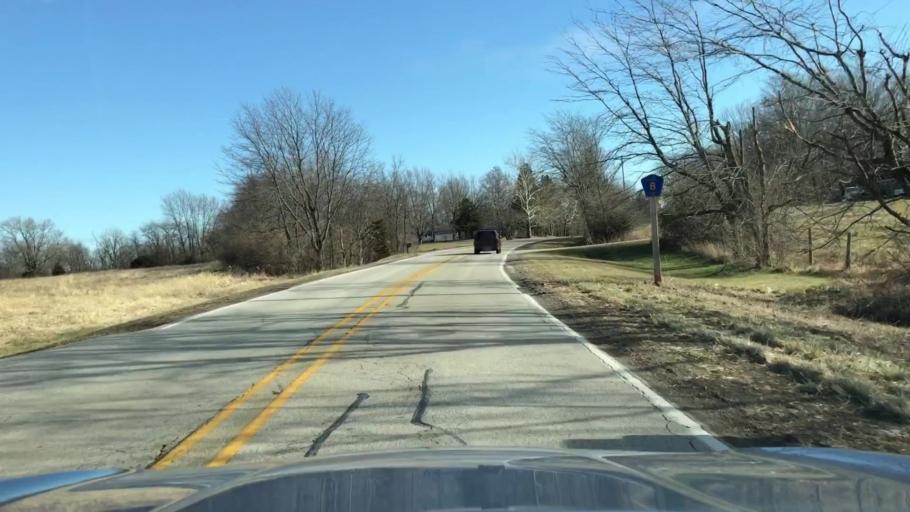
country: US
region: Illinois
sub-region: McLean County
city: Lexington
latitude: 40.6478
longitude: -88.8415
